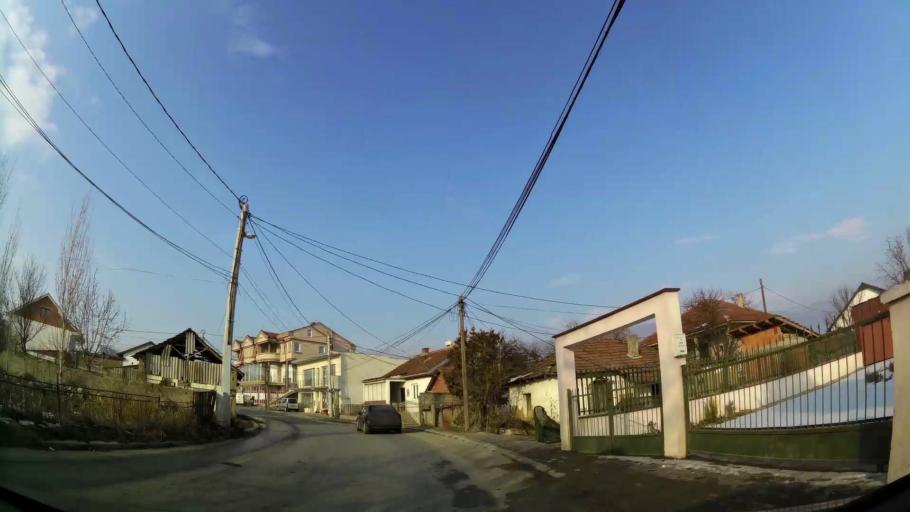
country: MK
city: Creshevo
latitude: 42.0255
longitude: 21.5150
